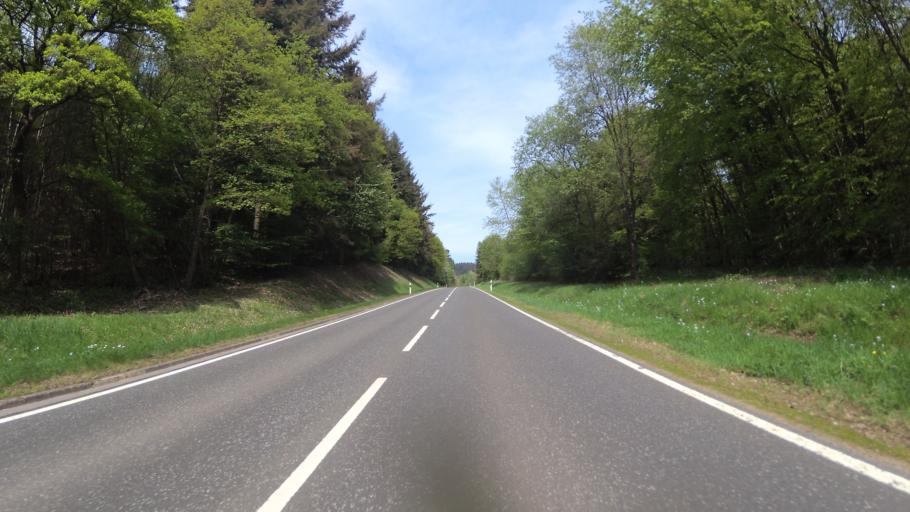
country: DE
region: Rheinland-Pfalz
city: Bausendorf
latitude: 50.0228
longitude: 6.9986
